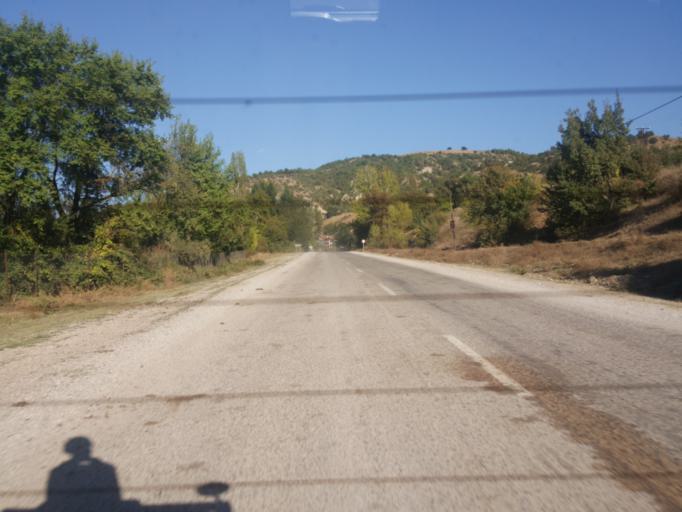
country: TR
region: Amasya
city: Tasova
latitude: 40.7395
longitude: 36.2777
